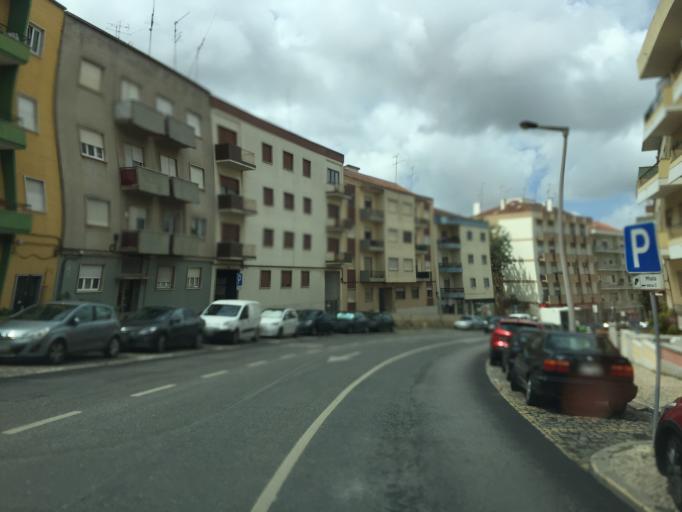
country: PT
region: Lisbon
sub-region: Torres Vedras
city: Torres Vedras
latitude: 39.0869
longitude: -9.2575
